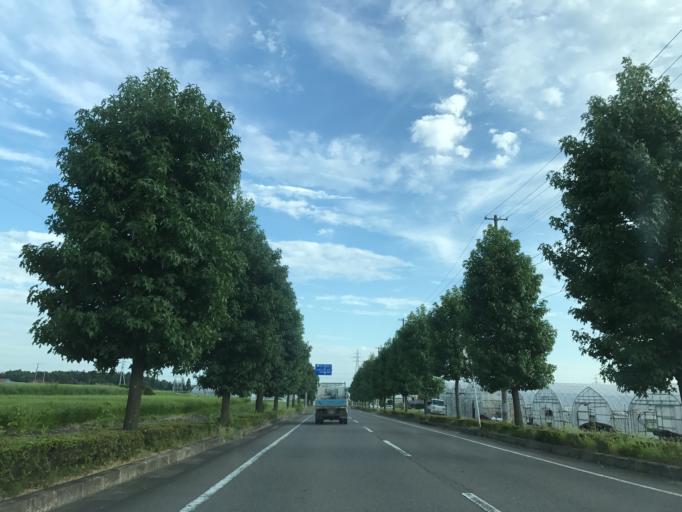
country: JP
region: Fukushima
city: Sukagawa
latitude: 37.3360
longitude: 140.3392
